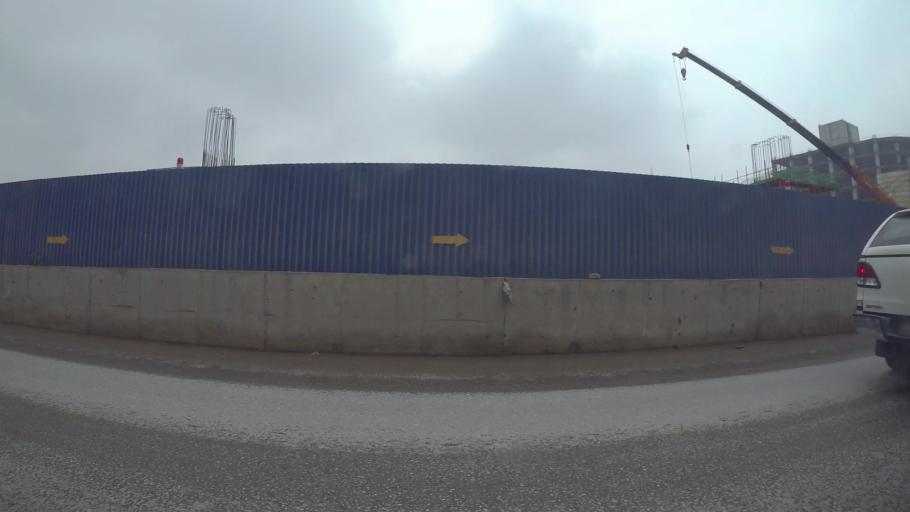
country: VN
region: Ha Noi
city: Cau Dien
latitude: 21.0548
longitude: 105.7818
